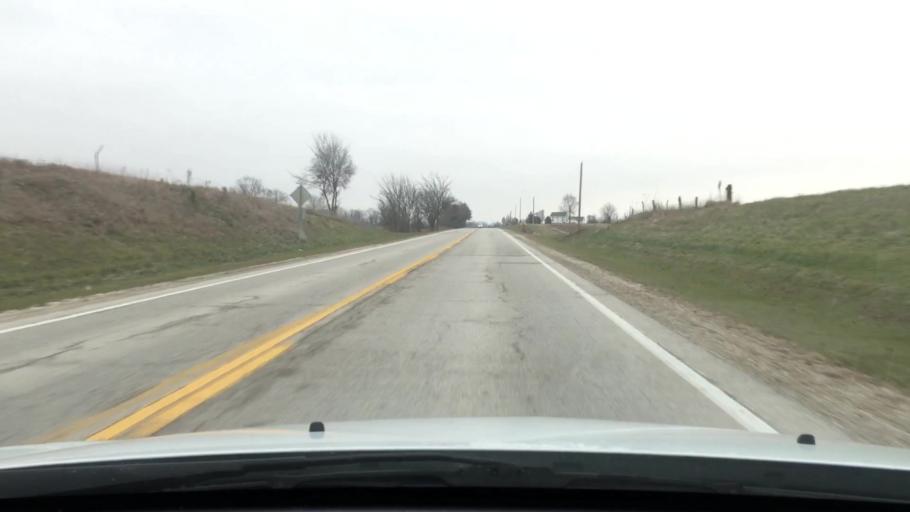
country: US
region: Illinois
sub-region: Pike County
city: Pittsfield
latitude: 39.5933
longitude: -90.8939
